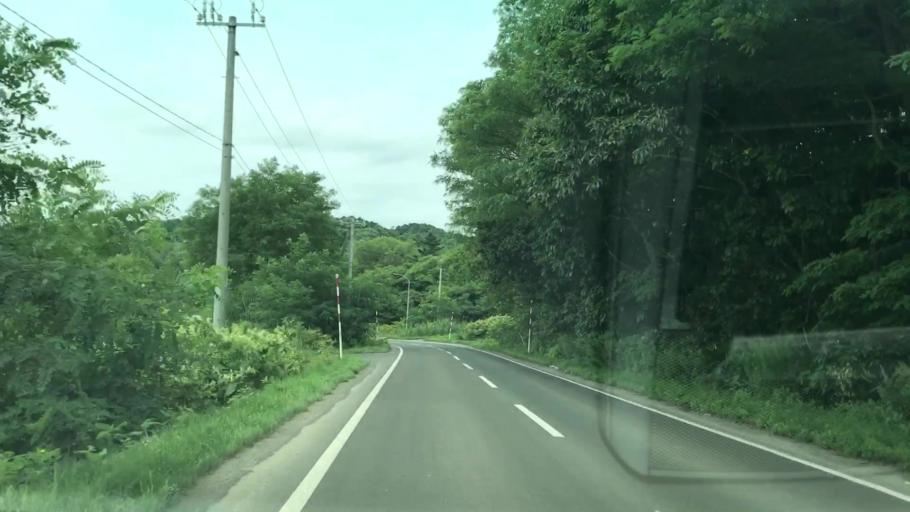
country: JP
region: Hokkaido
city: Iwanai
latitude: 43.0376
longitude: 140.5455
